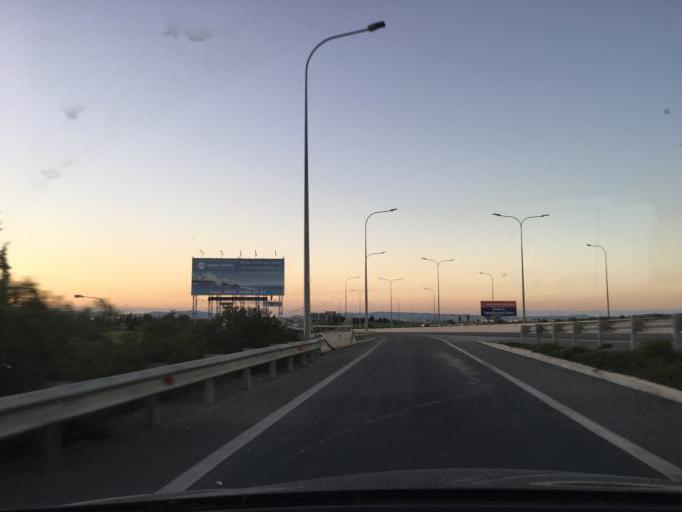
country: CY
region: Larnaka
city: Dhromolaxia
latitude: 34.8770
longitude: 33.6007
